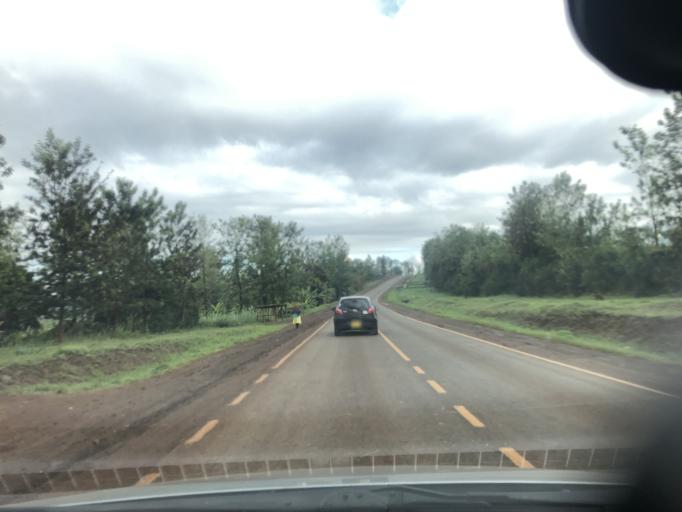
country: KE
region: Murang'a District
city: Maragua
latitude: -0.8315
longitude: 37.1374
